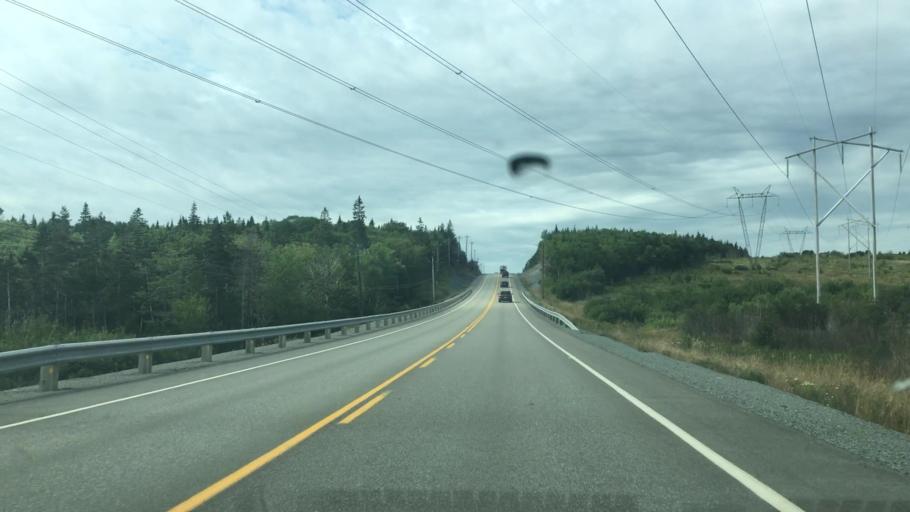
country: CA
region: Nova Scotia
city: Princeville
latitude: 45.6735
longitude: -60.7941
